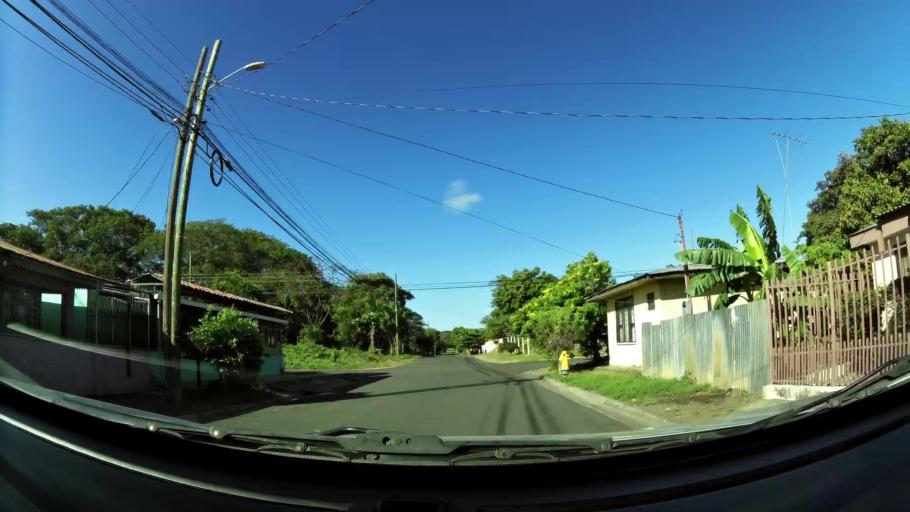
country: CR
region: Guanacaste
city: Belen
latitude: 10.4434
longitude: -85.5523
